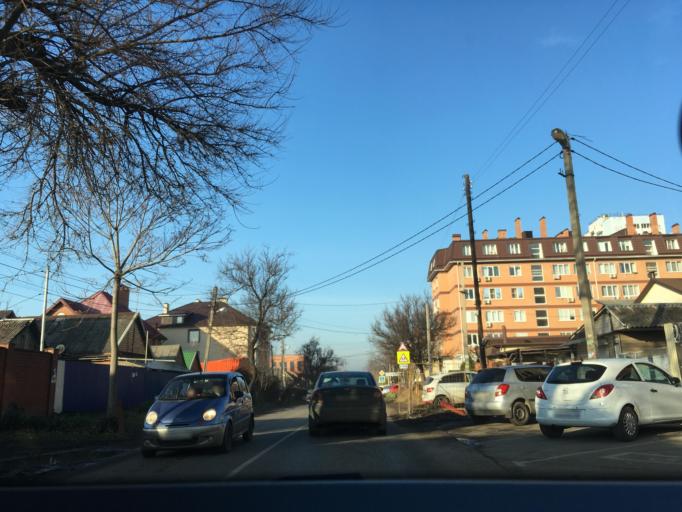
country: RU
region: Krasnodarskiy
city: Krasnodar
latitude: 45.0678
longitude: 39.0217
